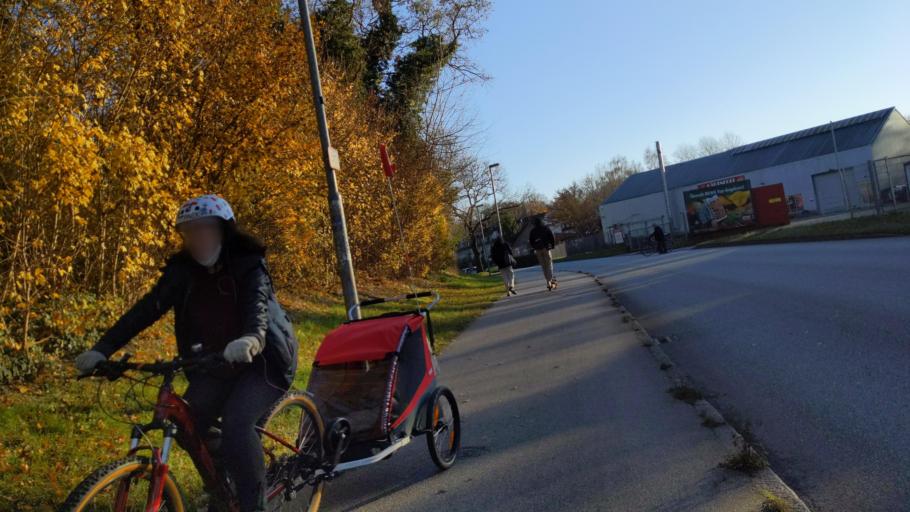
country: DE
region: Schleswig-Holstein
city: Luebeck
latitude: 53.8901
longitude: 10.7086
